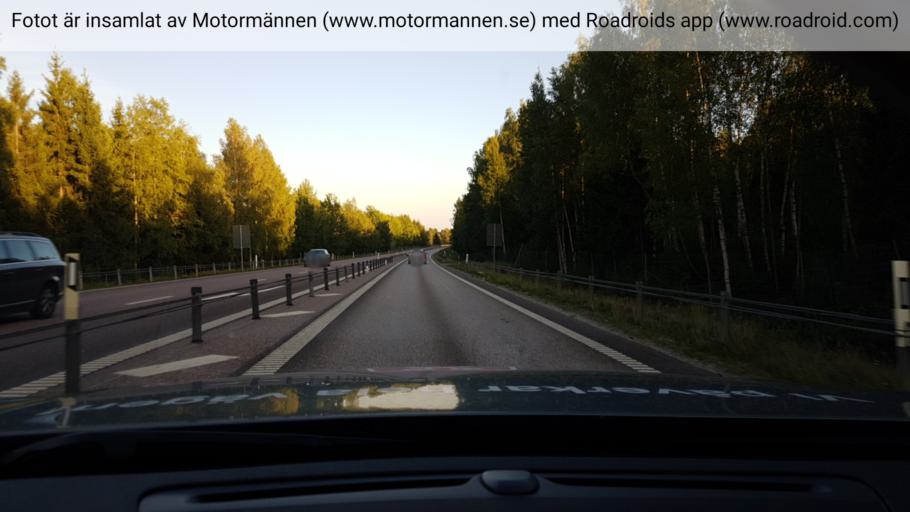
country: SE
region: Vaestmanland
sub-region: Surahammars Kommun
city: Ramnas
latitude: 59.8103
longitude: 16.1347
